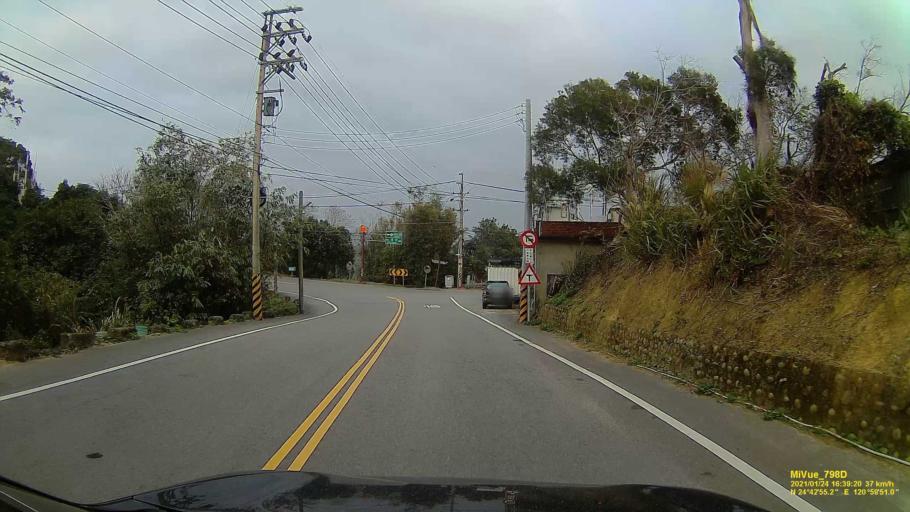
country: TW
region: Taiwan
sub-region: Hsinchu
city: Hsinchu
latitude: 24.7151
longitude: 120.9974
